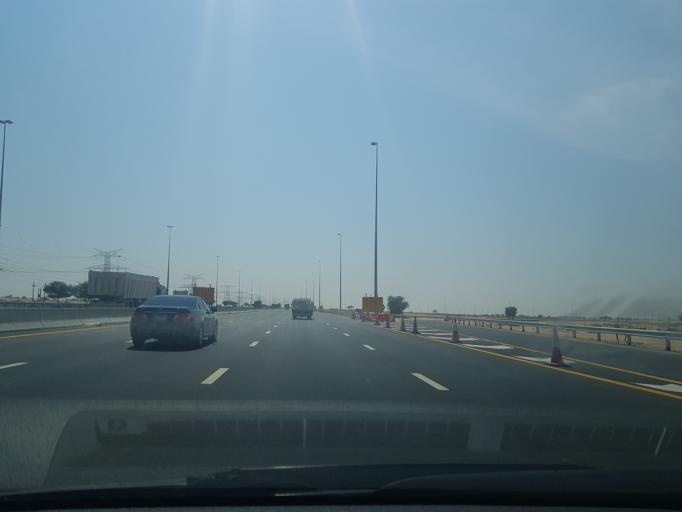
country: AE
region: Ash Shariqah
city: Sharjah
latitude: 25.2294
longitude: 55.5617
